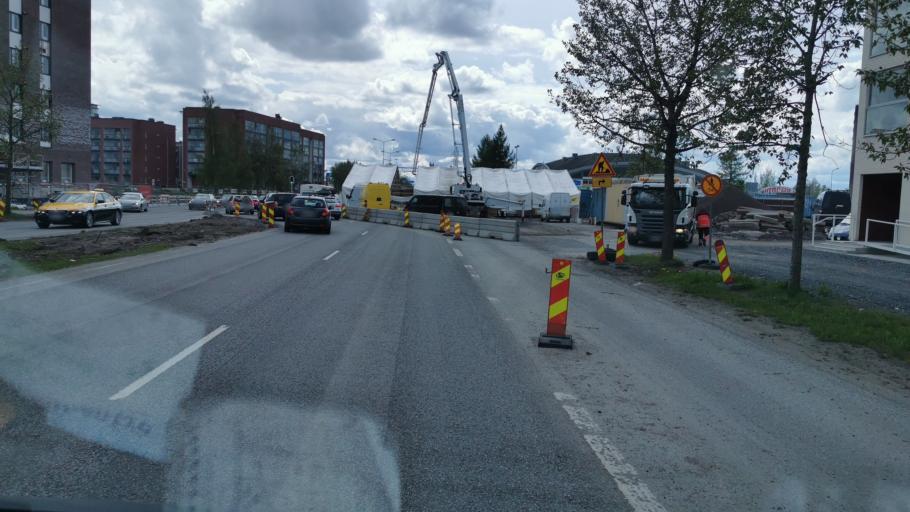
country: FI
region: Northern Ostrobothnia
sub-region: Oulu
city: Oulu
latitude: 65.0016
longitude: 25.4635
